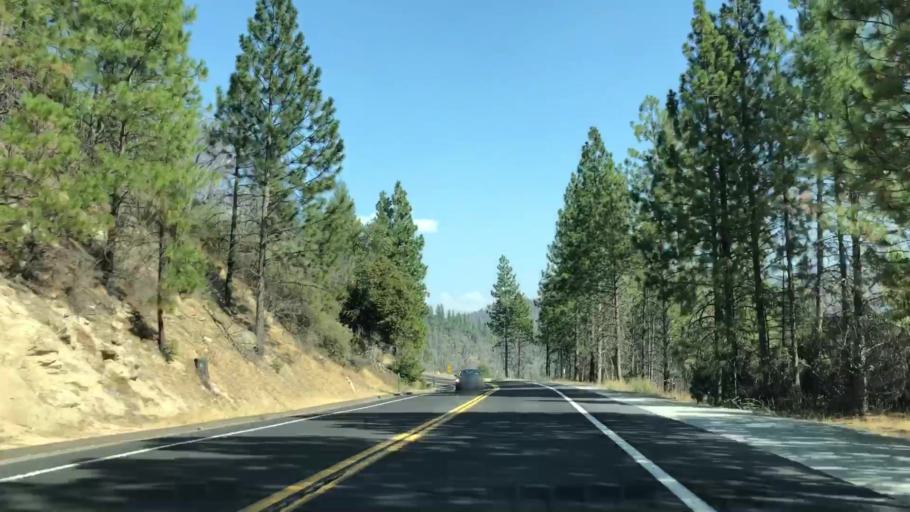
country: US
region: California
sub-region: Mariposa County
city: Midpines
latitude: 37.8161
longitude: -119.9376
